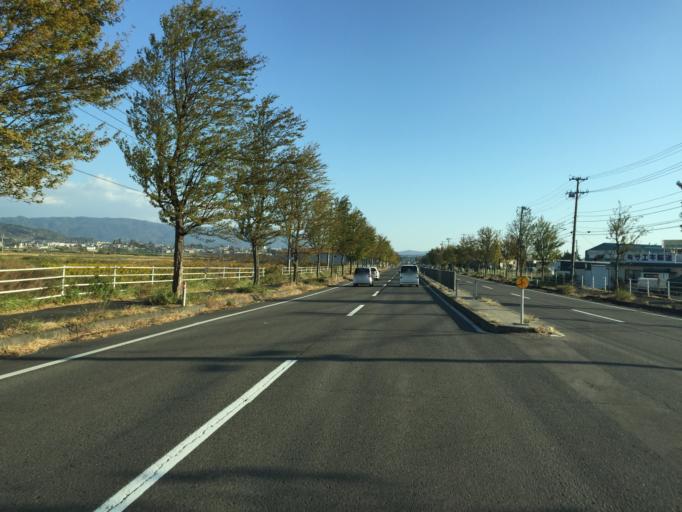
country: JP
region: Fukushima
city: Hobaramachi
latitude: 37.8267
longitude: 140.5106
